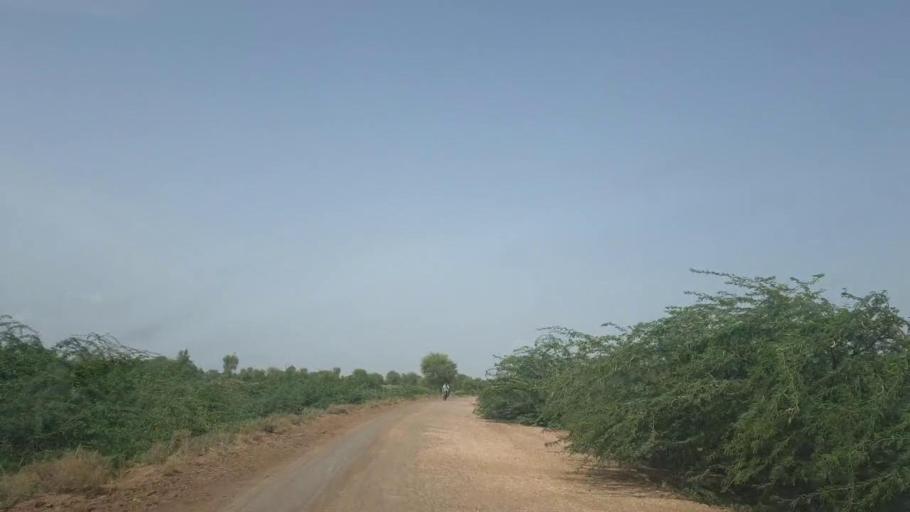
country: PK
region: Sindh
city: Tando Bago
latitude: 24.7955
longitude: 69.1513
